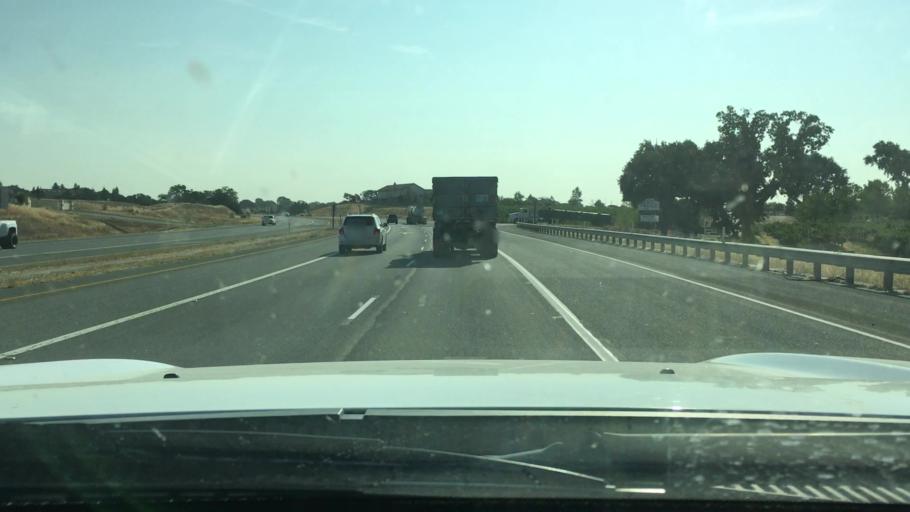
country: US
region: California
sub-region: San Luis Obispo County
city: Paso Robles
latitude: 35.6444
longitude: -120.6358
